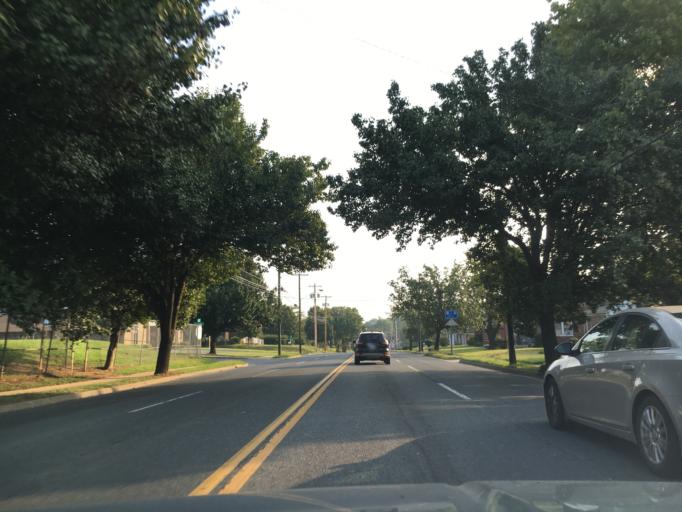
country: US
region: Virginia
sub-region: City of Lynchburg
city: West Lynchburg
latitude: 37.3811
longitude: -79.1817
